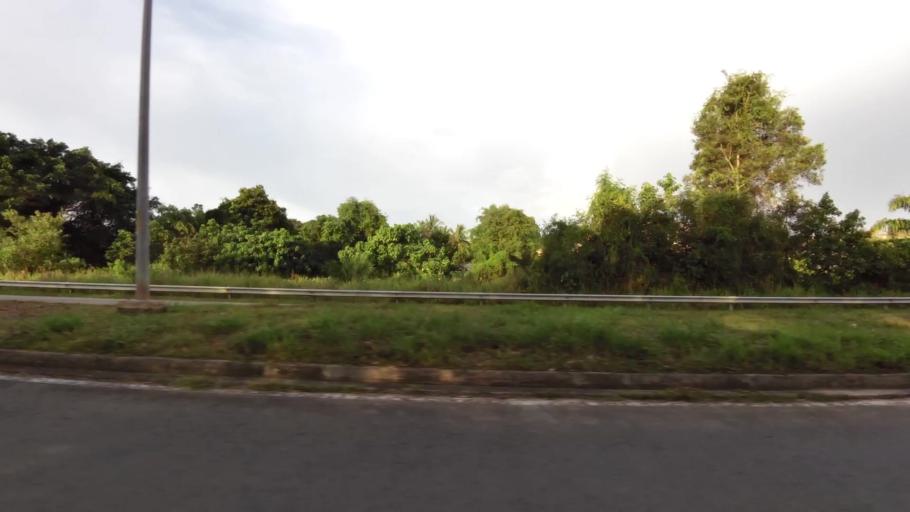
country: BN
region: Brunei and Muara
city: Bandar Seri Begawan
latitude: 4.9863
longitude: 114.9907
